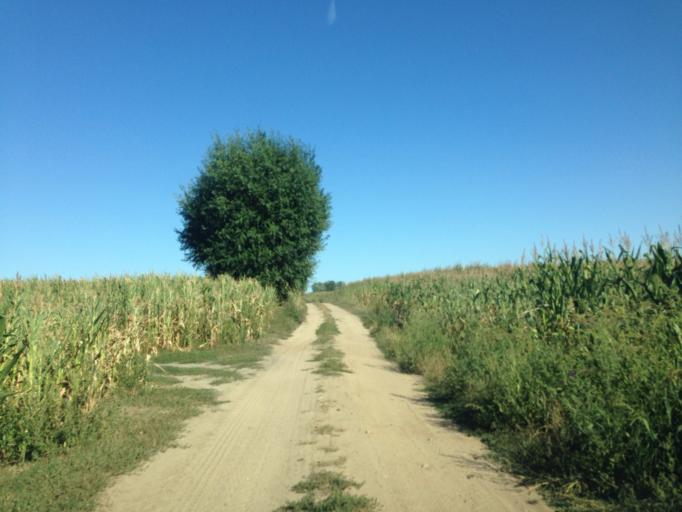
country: PL
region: Kujawsko-Pomorskie
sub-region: Powiat brodnicki
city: Brodnica
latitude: 53.2114
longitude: 19.4094
